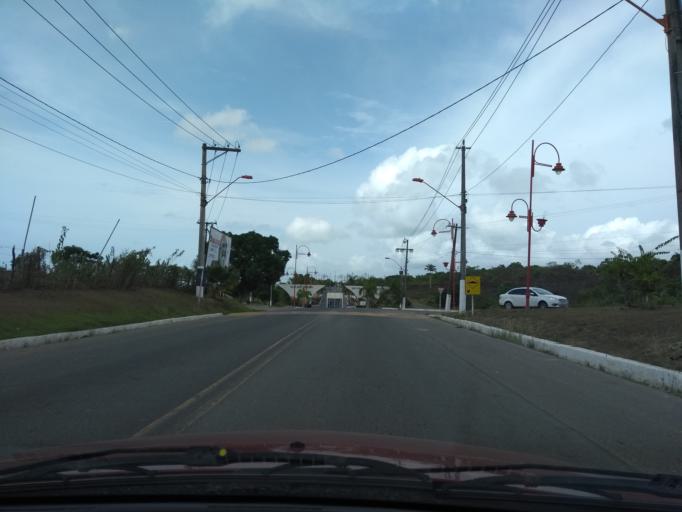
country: BR
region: Bahia
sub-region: Sao Francisco Do Conde
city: Sao Francisco do Conde
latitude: -12.6122
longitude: -38.6544
